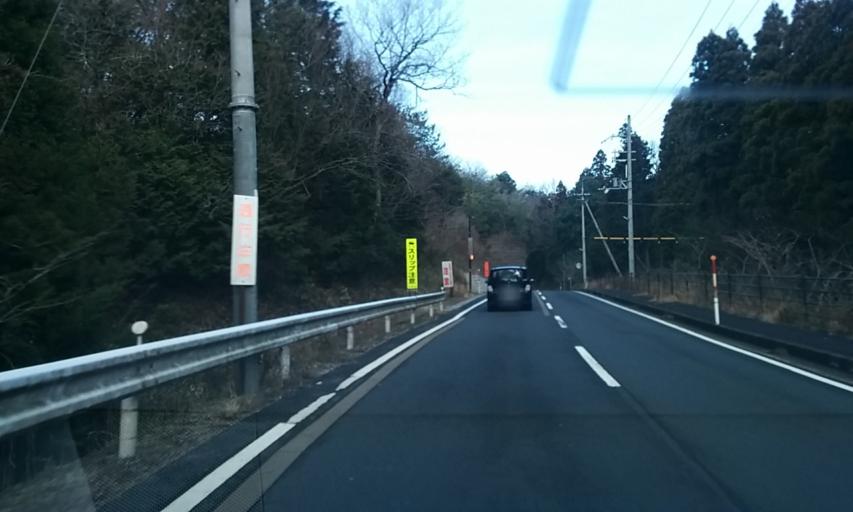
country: JP
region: Kyoto
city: Miyazu
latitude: 35.5804
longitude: 135.1182
